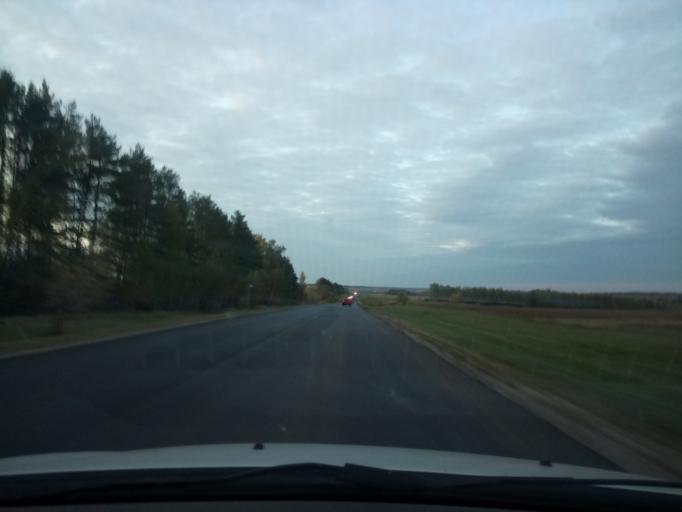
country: RU
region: Nizjnij Novgorod
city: Bol'shoye Murashkino
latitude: 55.8537
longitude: 44.7489
